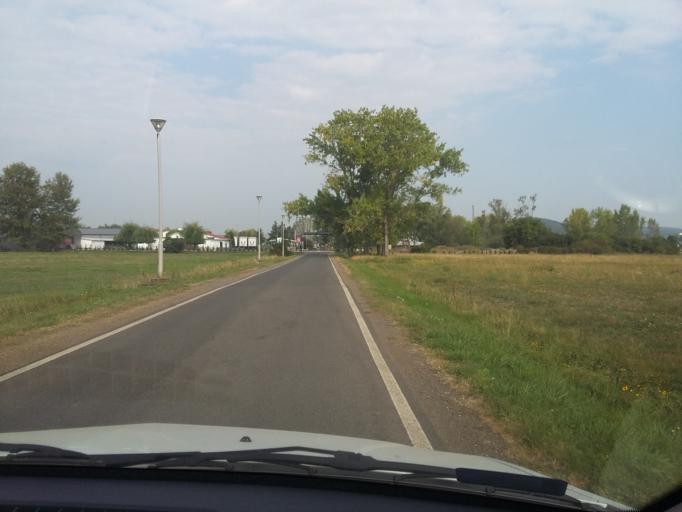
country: HU
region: Borsod-Abauj-Zemplen
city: Bekecs
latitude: 48.1406
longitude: 21.1599
